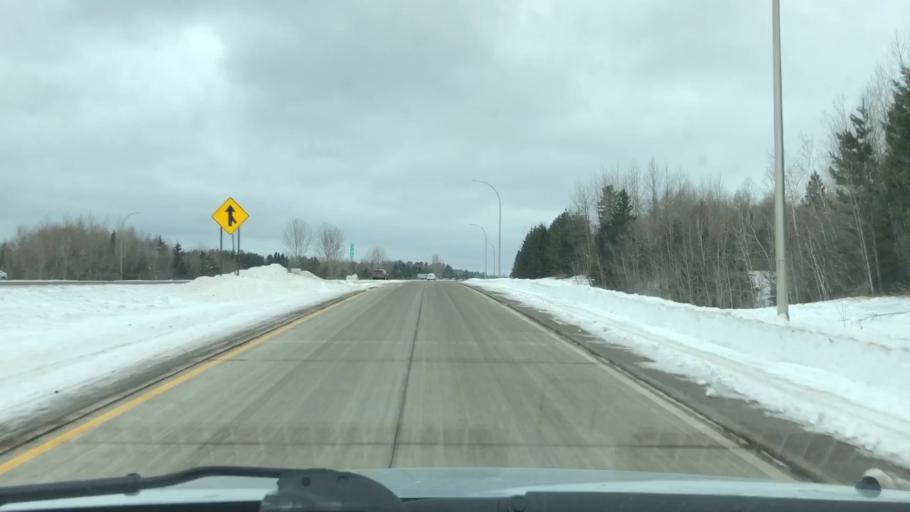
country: US
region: Minnesota
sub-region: Carlton County
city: Esko
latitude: 46.7031
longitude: -92.3051
